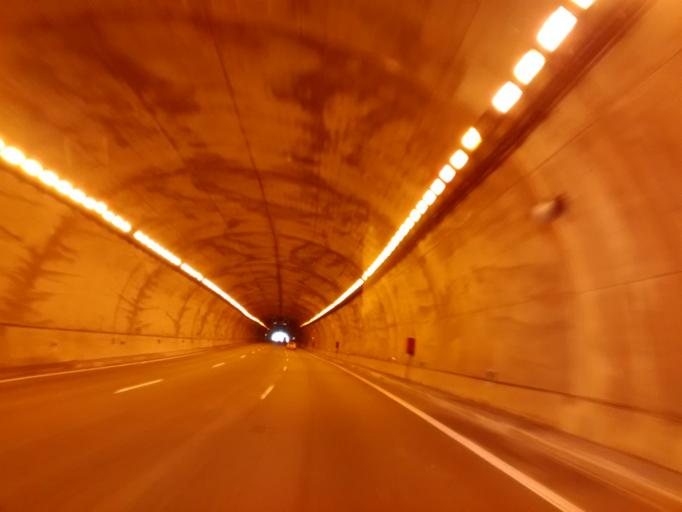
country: ES
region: Cantabria
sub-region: Provincia de Cantabria
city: Cartes
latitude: 43.3064
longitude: -4.0791
